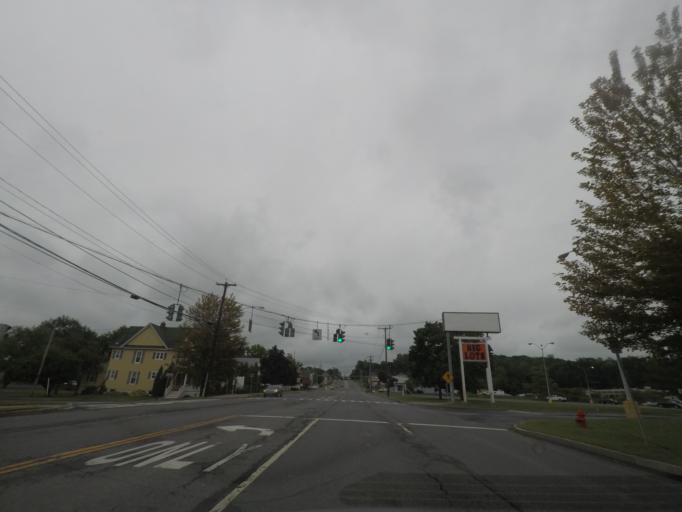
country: US
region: New York
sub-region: Rensselaer County
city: Hampton Manor
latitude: 42.6205
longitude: -73.7357
